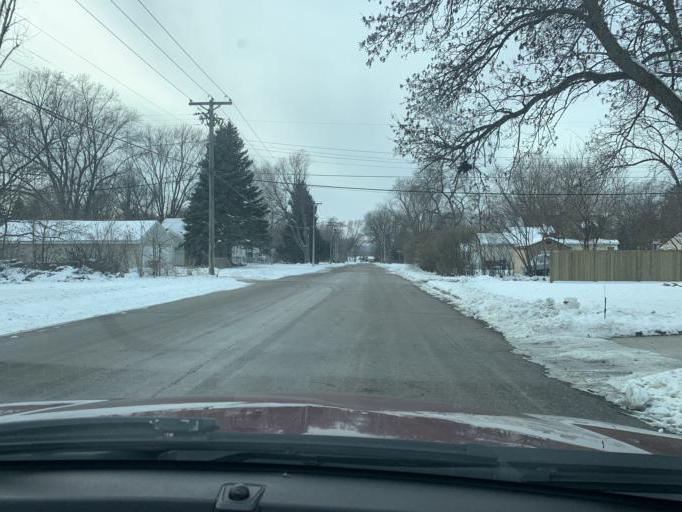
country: US
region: Minnesota
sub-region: Washington County
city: Saint Paul Park
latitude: 44.8441
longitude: -92.9873
